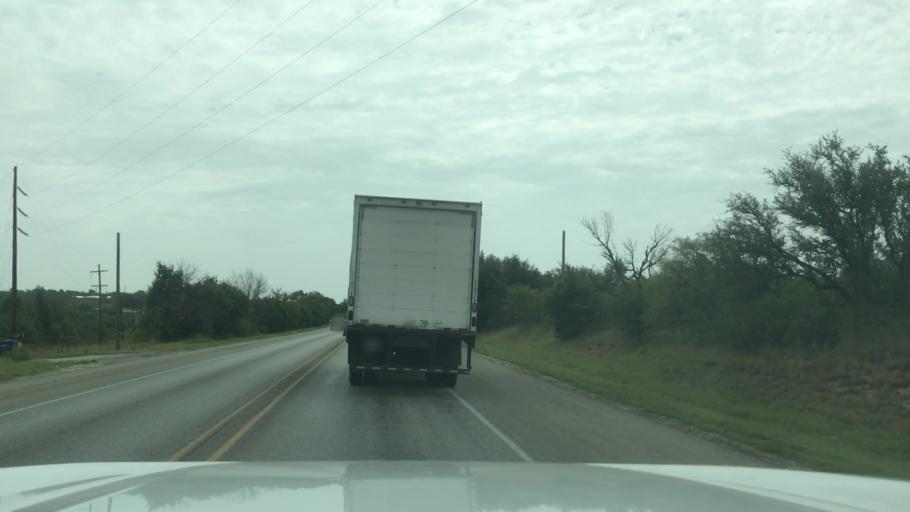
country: US
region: Texas
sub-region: Erath County
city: Dublin
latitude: 32.0894
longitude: -98.4373
